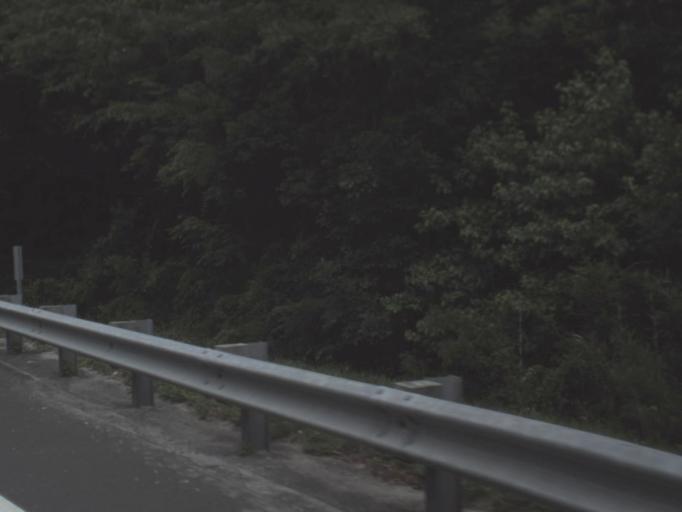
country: US
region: Florida
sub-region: Nassau County
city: Callahan
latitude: 30.5599
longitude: -81.8197
